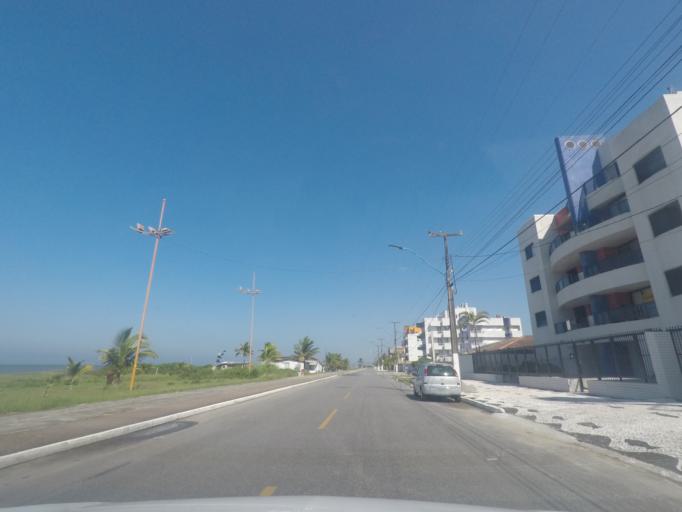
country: BR
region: Parana
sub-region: Pontal Do Parana
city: Pontal do Parana
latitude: -25.7247
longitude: -48.4850
